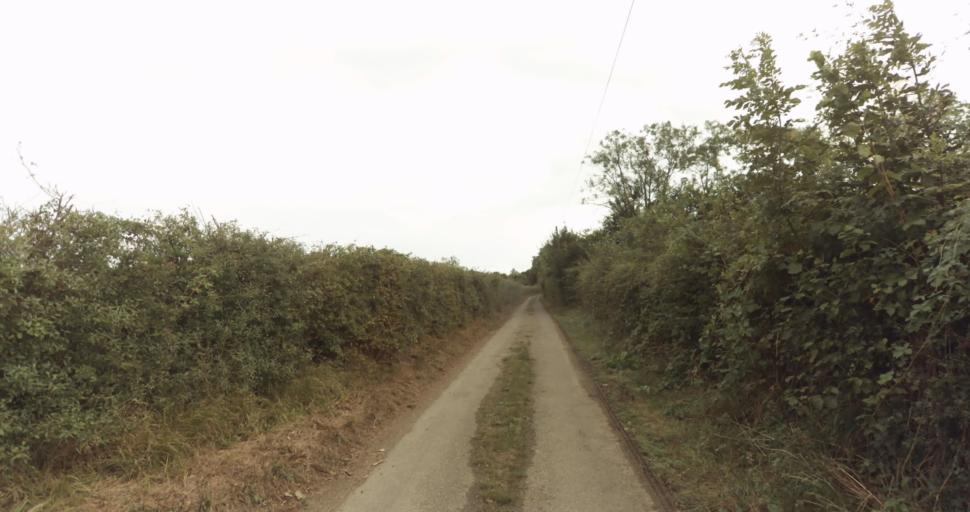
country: FR
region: Lower Normandy
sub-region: Departement de l'Orne
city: Gace
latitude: 48.8352
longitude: 0.2990
